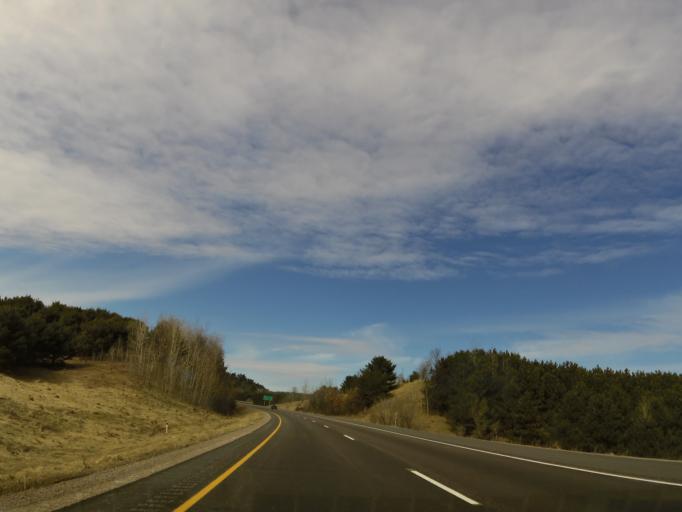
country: US
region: Wisconsin
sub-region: Trempealeau County
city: Osseo
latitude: 44.4717
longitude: -91.0992
